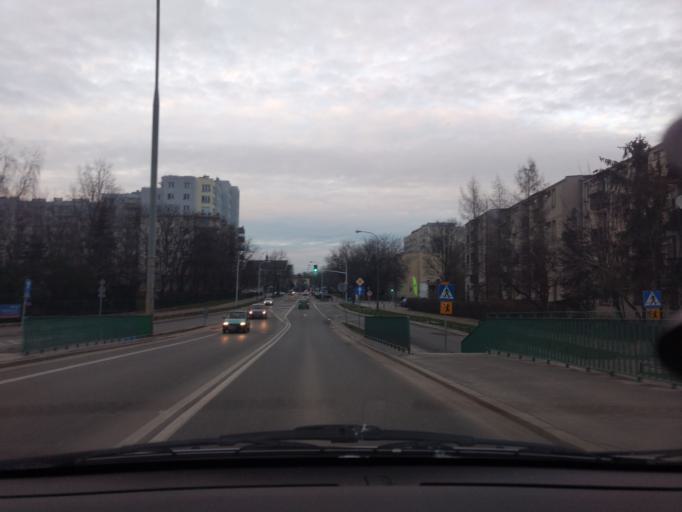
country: PL
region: Masovian Voivodeship
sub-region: Warszawa
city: Praga Poludnie
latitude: 52.2297
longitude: 21.0625
